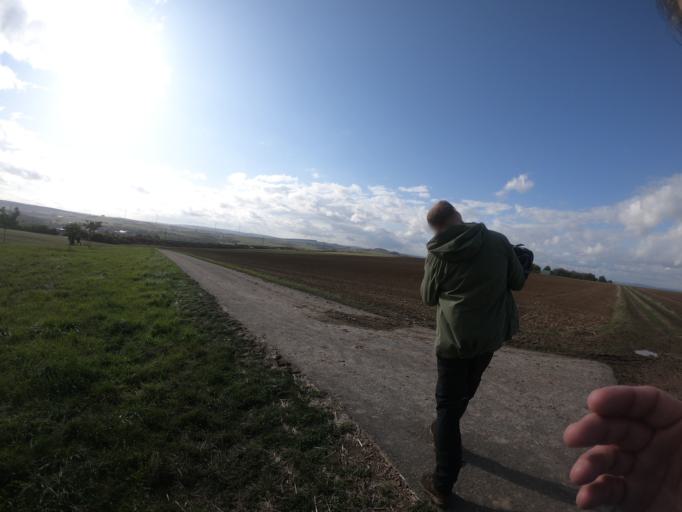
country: DE
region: Hesse
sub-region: Regierungsbezirk Giessen
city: Villmar
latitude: 50.3398
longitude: 8.1960
